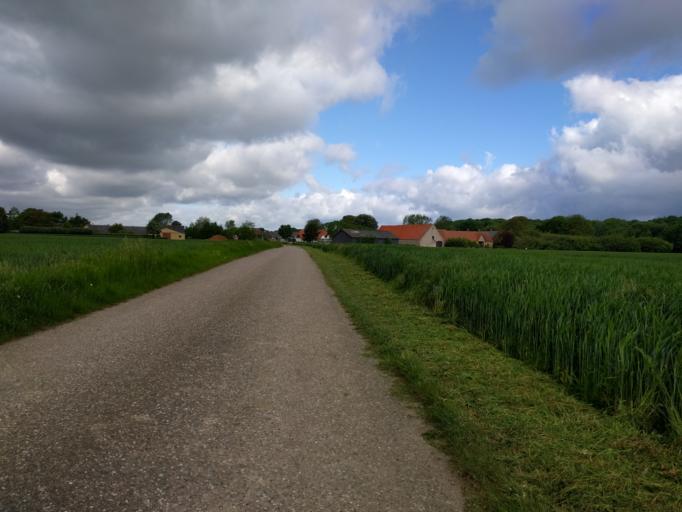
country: DK
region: South Denmark
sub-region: Kerteminde Kommune
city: Kerteminde
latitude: 55.4142
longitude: 10.6262
